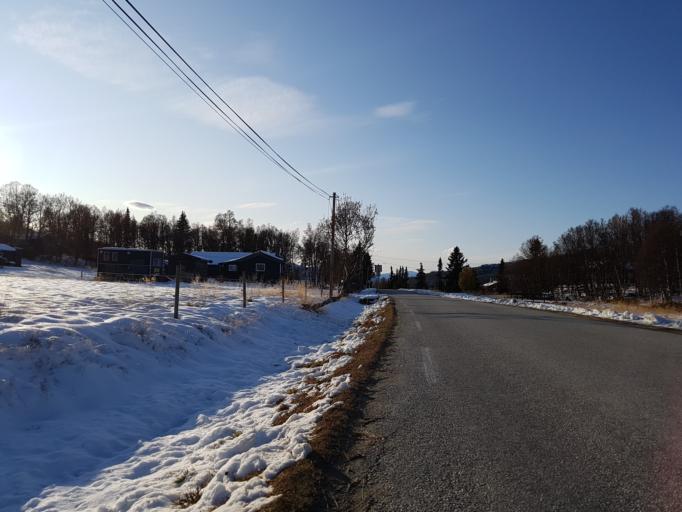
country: NO
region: Oppland
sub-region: Sel
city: Otta
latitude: 61.8090
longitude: 9.6816
